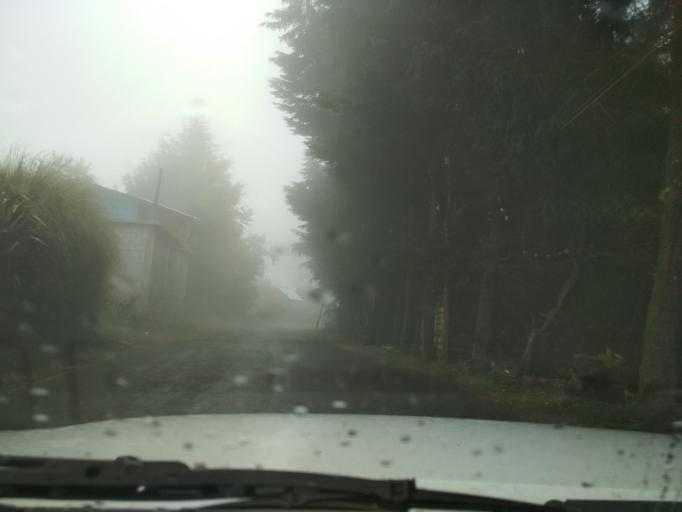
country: MX
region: Veracruz
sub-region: Mariano Escobedo
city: San Isidro el Berro
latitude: 18.9279
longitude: -97.2084
